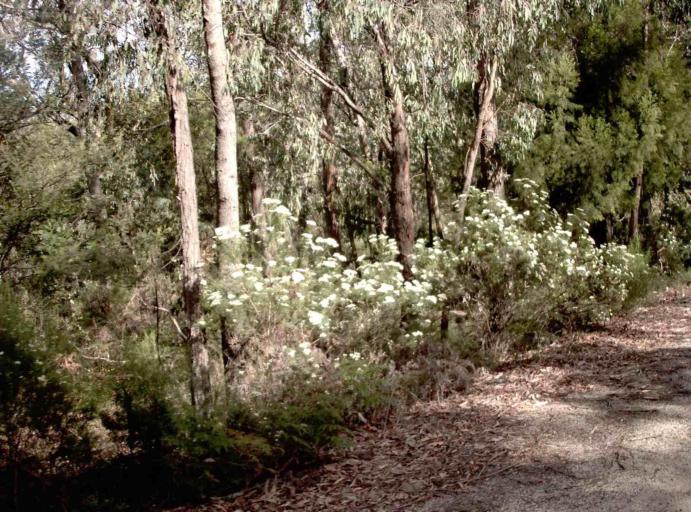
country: AU
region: Victoria
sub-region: East Gippsland
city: Lakes Entrance
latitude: -37.5462
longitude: 148.1478
